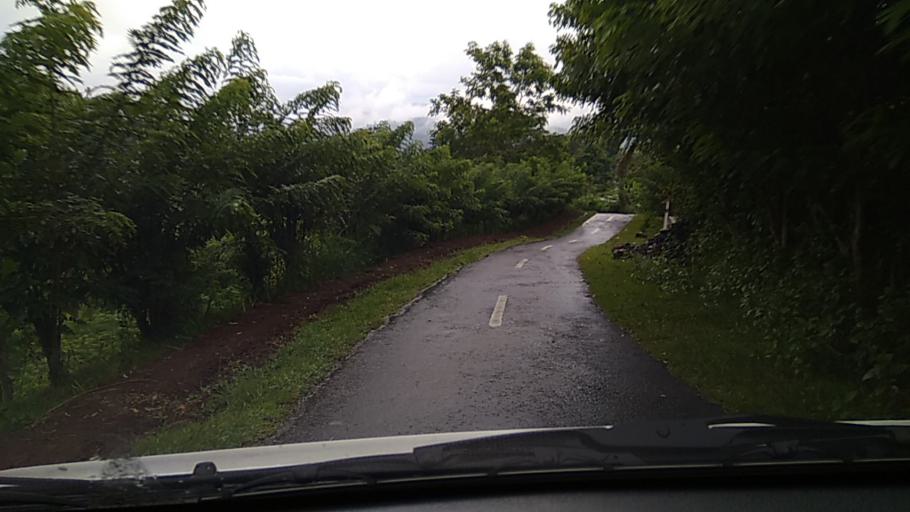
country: ID
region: Bali
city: Tiyingtali Kelod
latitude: -8.4029
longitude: 115.6298
